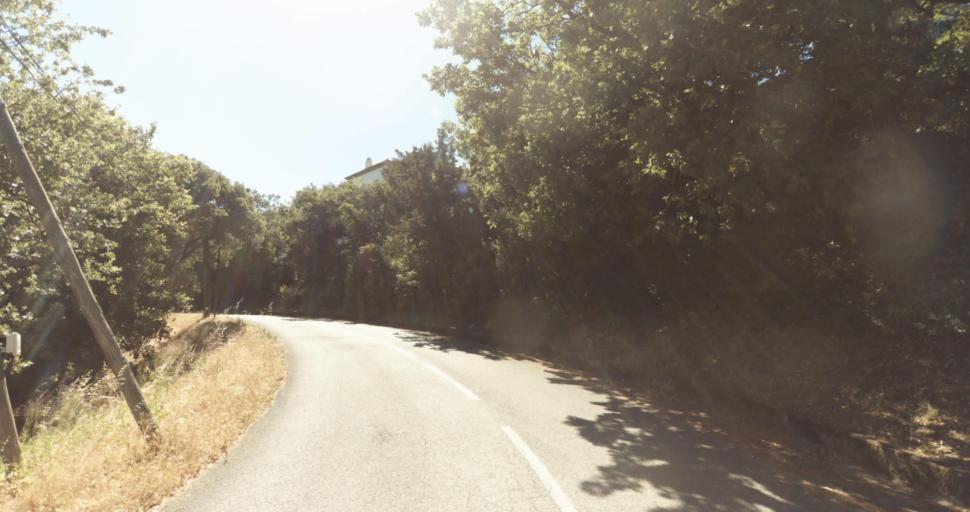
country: FR
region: Provence-Alpes-Cote d'Azur
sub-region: Departement du Var
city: Saint-Tropez
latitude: 43.2584
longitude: 6.6089
